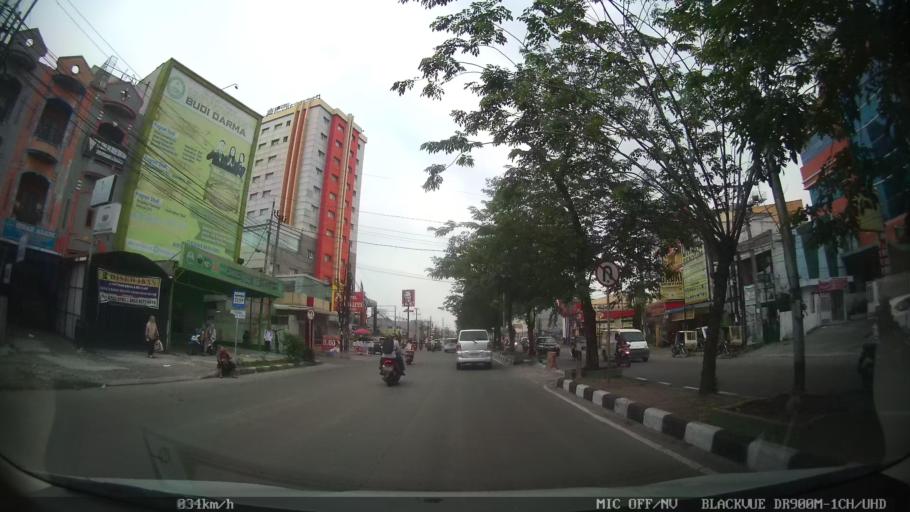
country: ID
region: North Sumatra
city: Medan
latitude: 3.5561
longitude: 98.6950
